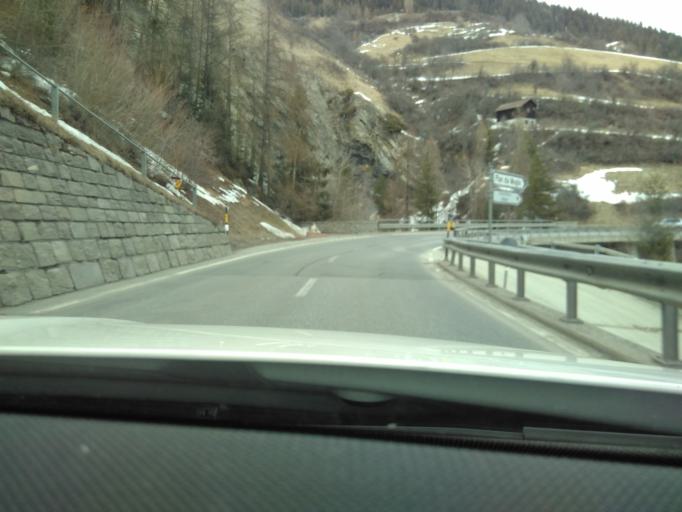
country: CH
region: Grisons
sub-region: Inn District
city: Scuol
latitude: 46.8313
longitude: 10.3757
